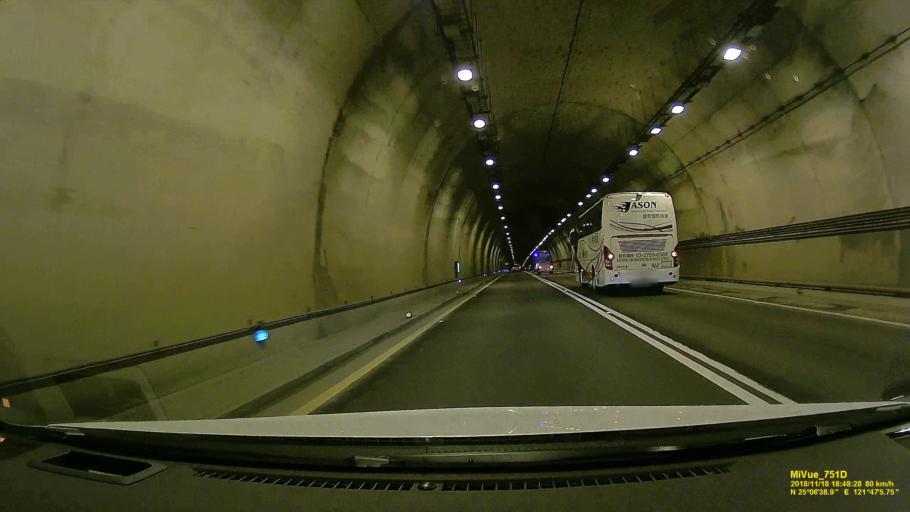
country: TW
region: Taiwan
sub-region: Keelung
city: Keelung
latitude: 25.1109
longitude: 121.7844
